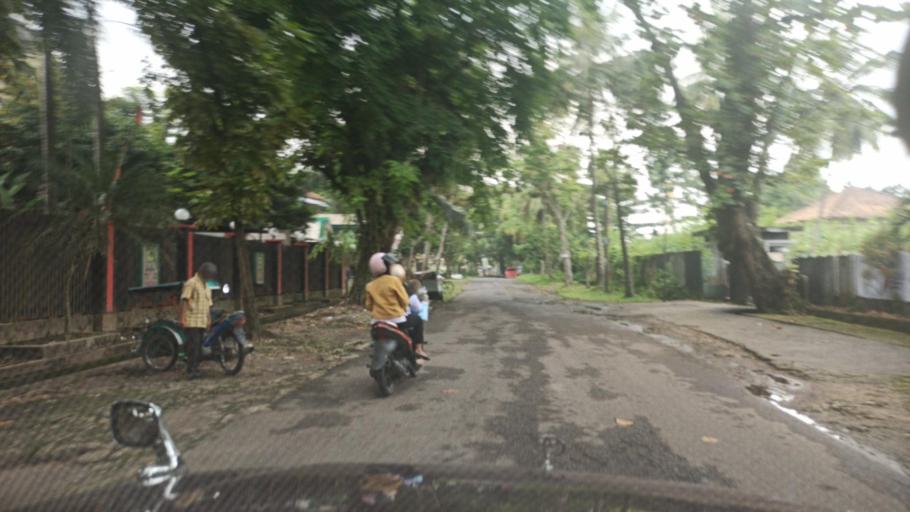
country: ID
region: South Sumatra
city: Plaju
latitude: -2.9916
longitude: 104.7476
